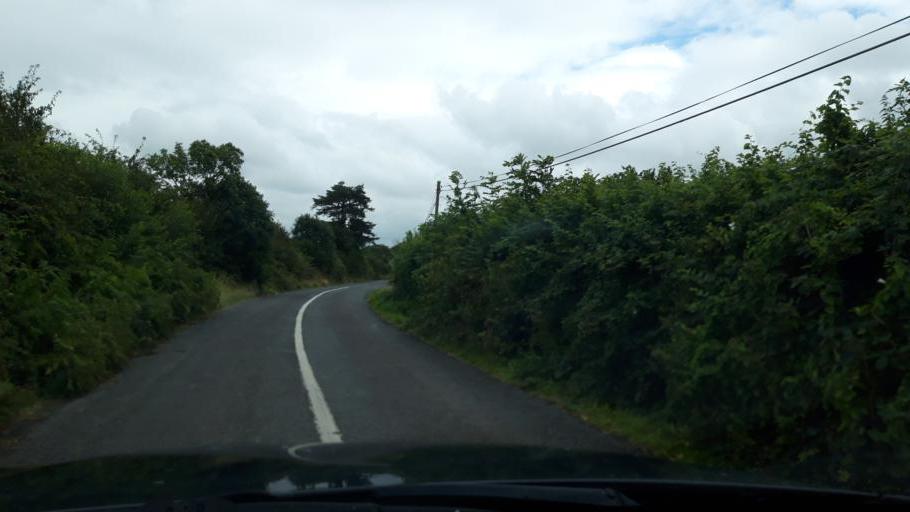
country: IE
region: Munster
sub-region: County Cork
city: Castlemartyr
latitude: 52.1298
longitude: -8.0020
